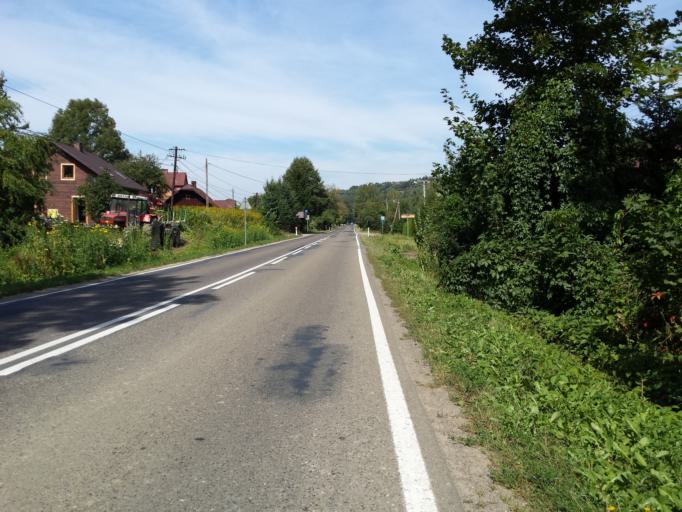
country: PL
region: Subcarpathian Voivodeship
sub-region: Powiat leski
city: Lesko
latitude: 49.4498
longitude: 22.3462
